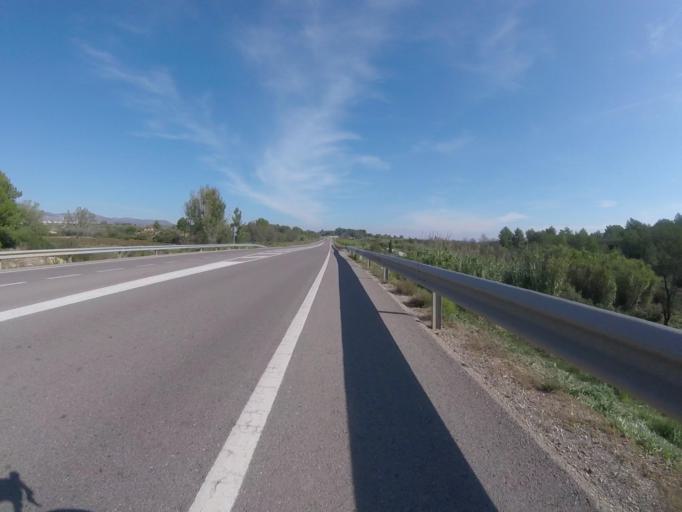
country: ES
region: Valencia
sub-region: Provincia de Castello
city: Benlloch
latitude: 40.2536
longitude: 0.0751
